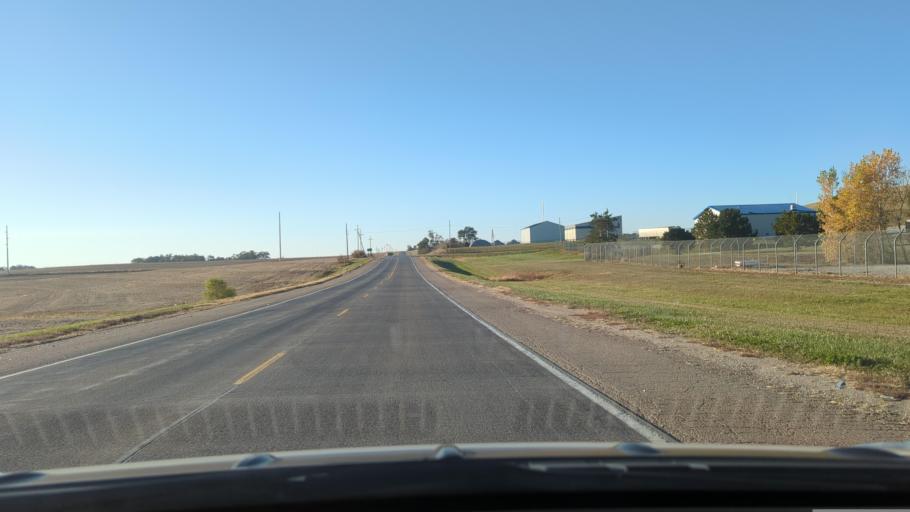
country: US
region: Nebraska
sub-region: Sarpy County
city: Springfield
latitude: 41.1012
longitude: -96.1577
